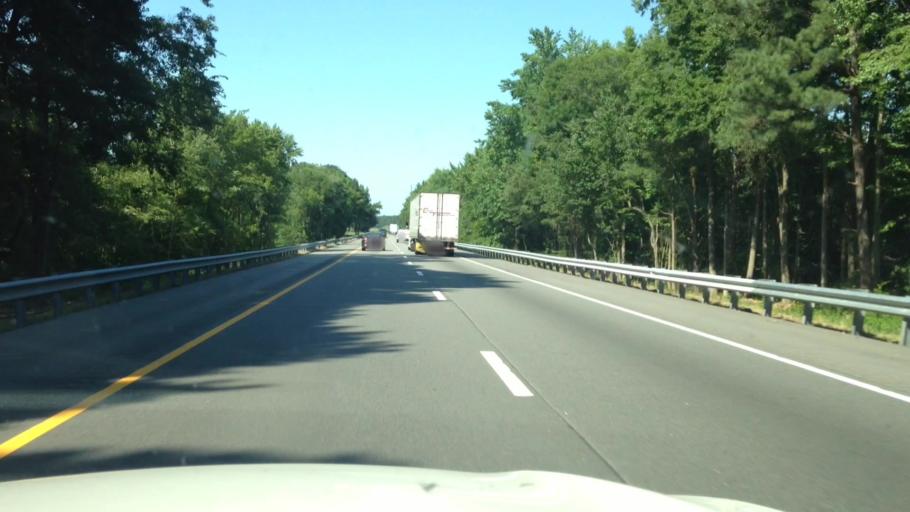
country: US
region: North Carolina
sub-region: Halifax County
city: Enfield
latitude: 36.1658
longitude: -77.7769
